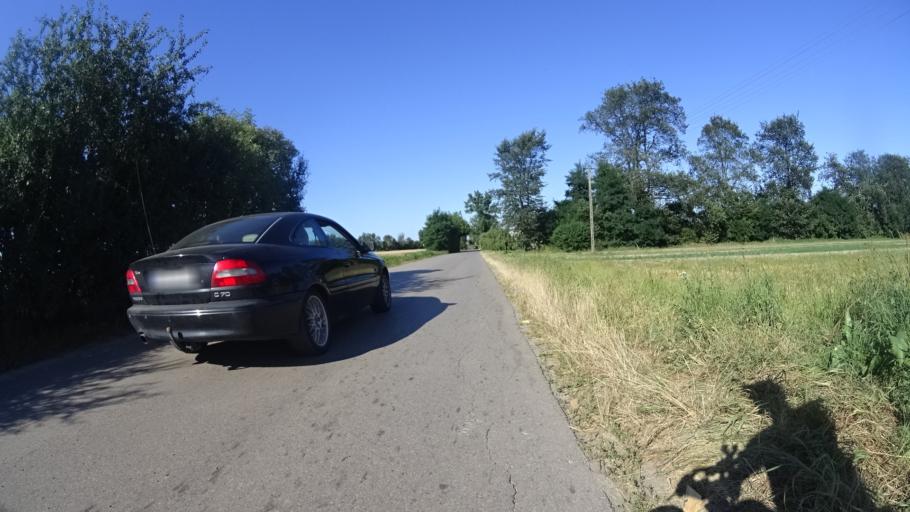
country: PL
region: Masovian Voivodeship
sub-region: Powiat bialobrzeski
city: Wysmierzyce
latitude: 51.6585
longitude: 20.8271
